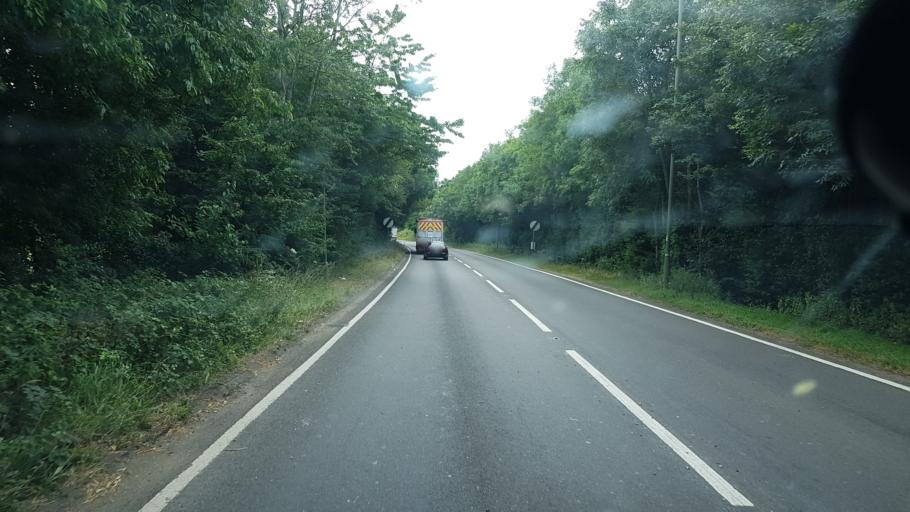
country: GB
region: England
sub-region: Surrey
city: Godstone
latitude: 51.2492
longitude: -0.0529
